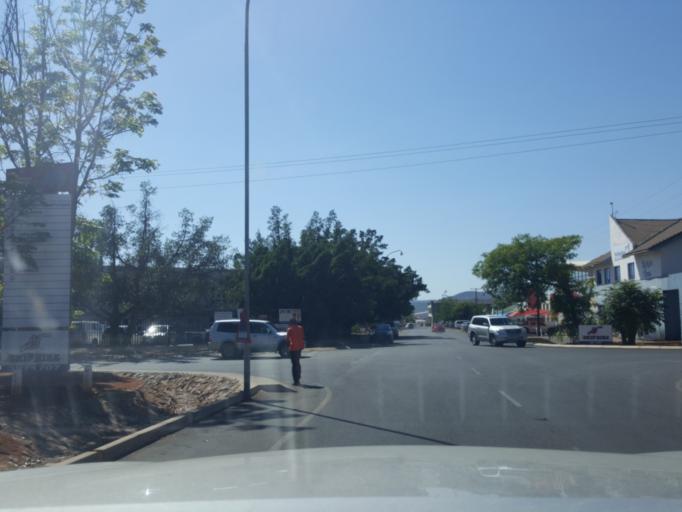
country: BW
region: South East
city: Gaborone
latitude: -24.6925
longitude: 25.8830
